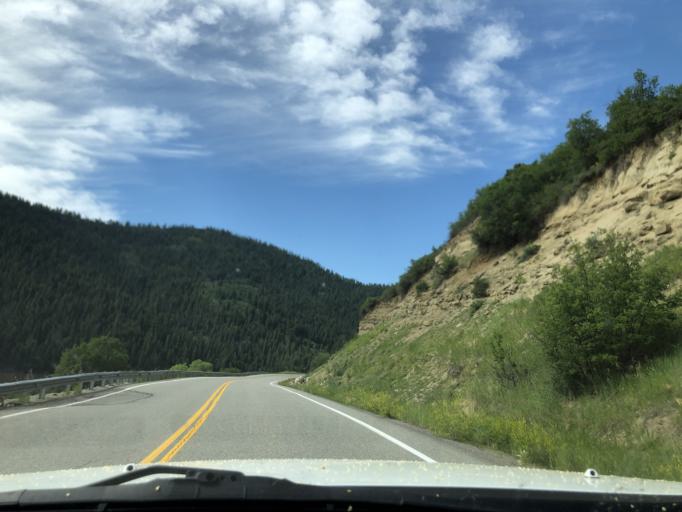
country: US
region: Colorado
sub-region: Delta County
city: Paonia
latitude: 38.9516
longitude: -107.3452
